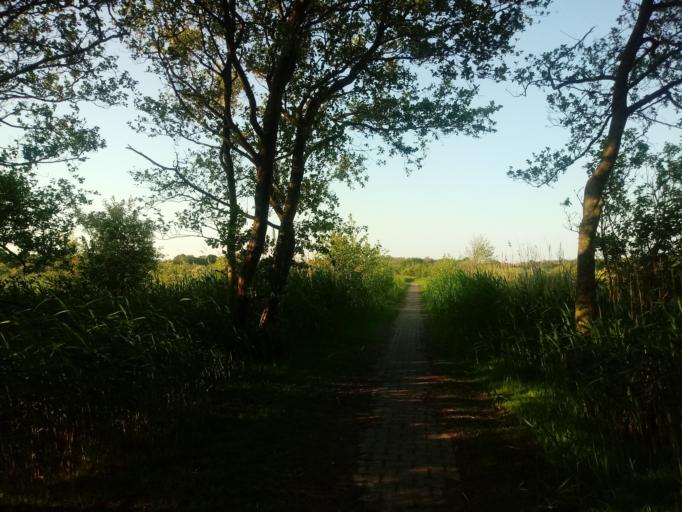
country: DE
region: Lower Saxony
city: Baltrum
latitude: 53.7289
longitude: 7.3952
